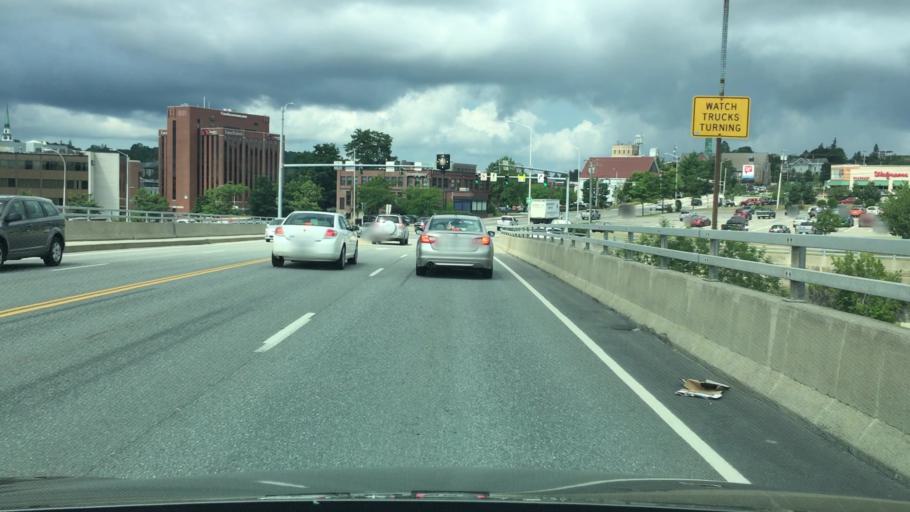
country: US
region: Maine
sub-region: Penobscot County
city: Brewer
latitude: 44.7996
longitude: -68.7649
